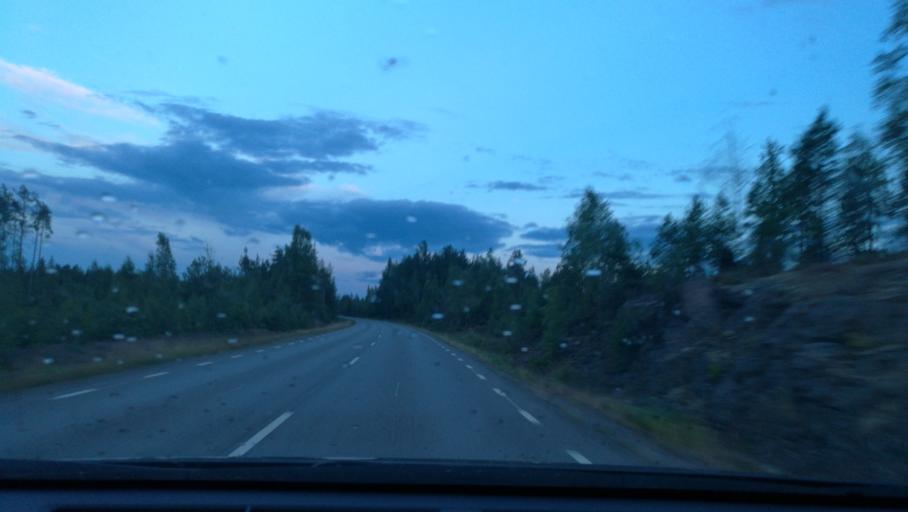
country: SE
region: OEstergoetland
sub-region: Norrkopings Kommun
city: Svartinge
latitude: 58.8027
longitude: 15.9431
